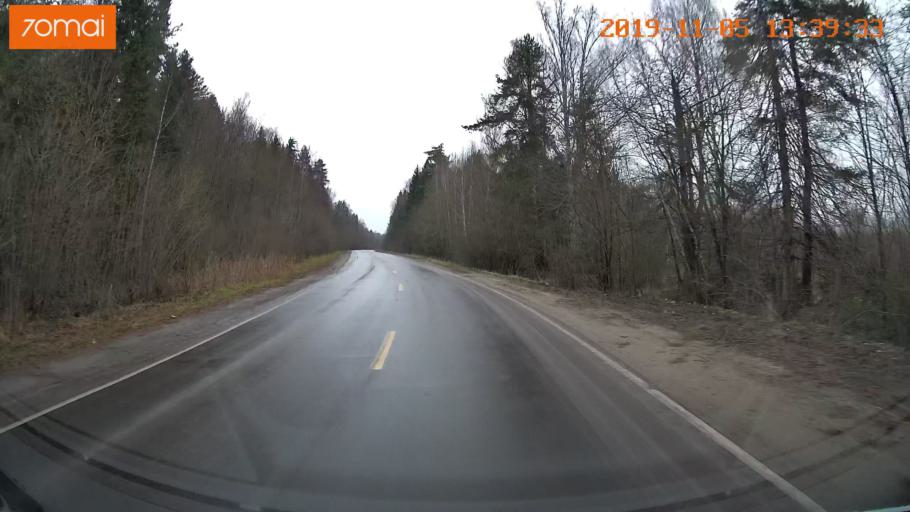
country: RU
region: Ivanovo
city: Shuya
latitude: 56.9406
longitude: 41.3863
